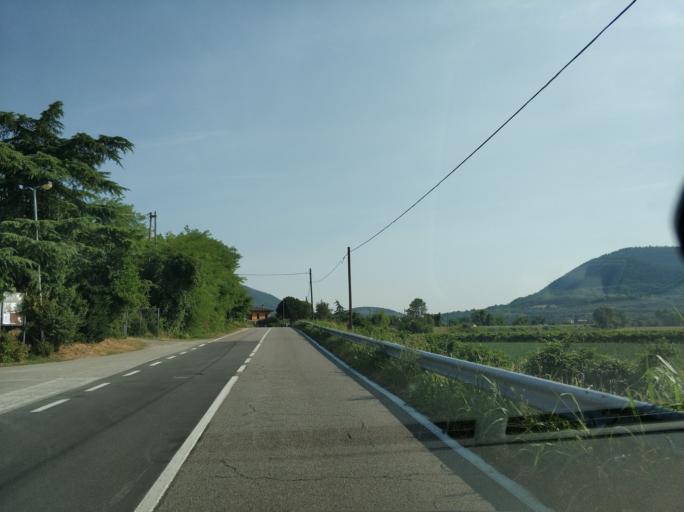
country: IT
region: Veneto
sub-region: Provincia di Padova
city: Arqua Petrarca
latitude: 45.2462
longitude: 11.7121
